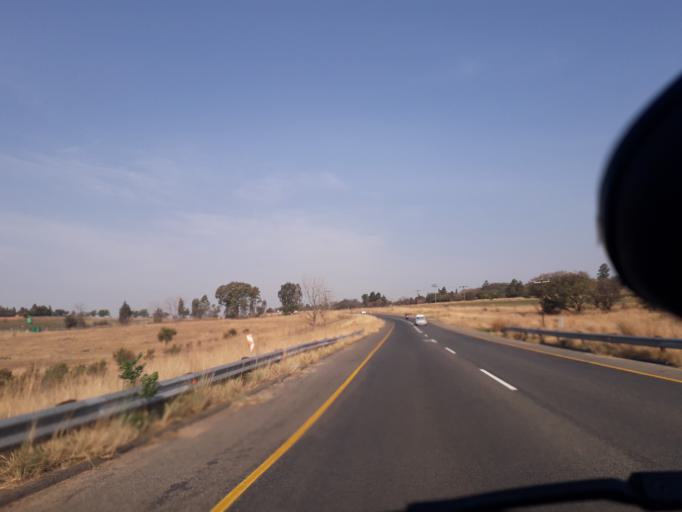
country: ZA
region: Gauteng
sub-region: West Rand District Municipality
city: Muldersdriseloop
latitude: -25.9688
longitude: 27.9064
